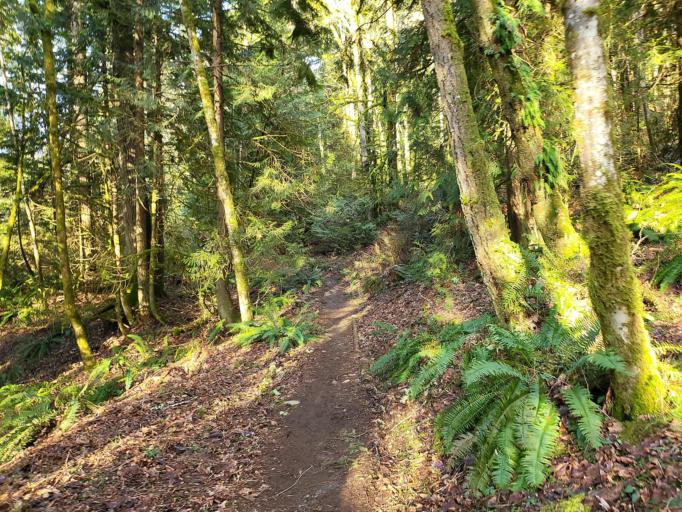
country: US
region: Washington
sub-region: King County
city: Issaquah
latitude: 47.5230
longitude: -122.0237
